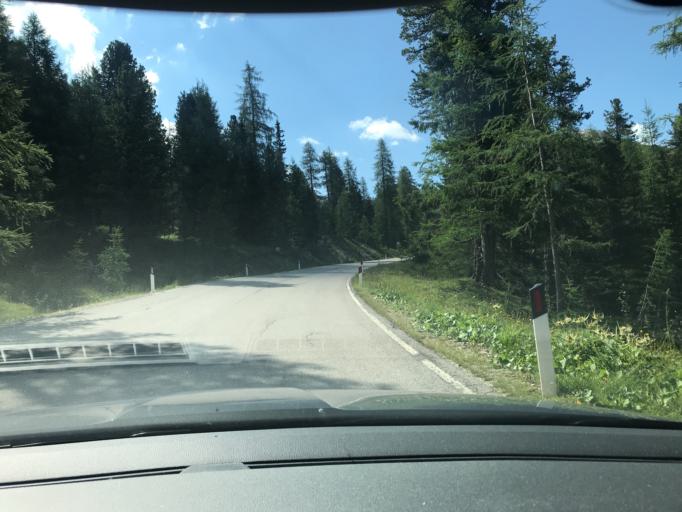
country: IT
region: Veneto
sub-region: Provincia di Belluno
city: Livinallongo del Col di Lana
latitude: 46.5395
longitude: 11.9842
